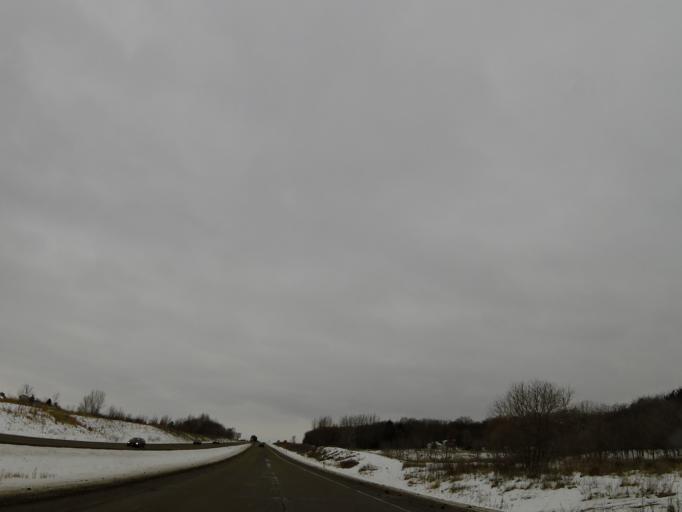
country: US
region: Minnesota
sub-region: Washington County
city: Stillwater
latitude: 45.0780
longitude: -92.7522
